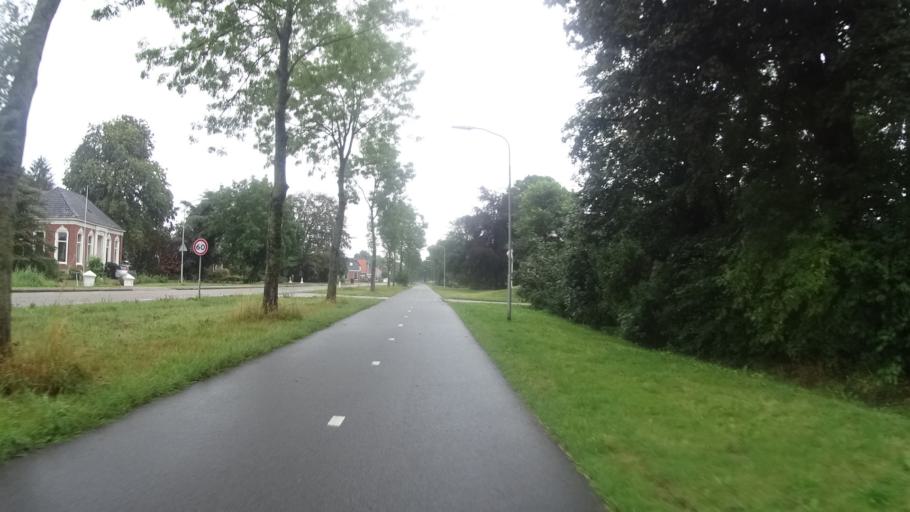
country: NL
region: Groningen
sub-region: Gemeente  Oldambt
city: Winschoten
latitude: 53.1618
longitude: 7.0821
